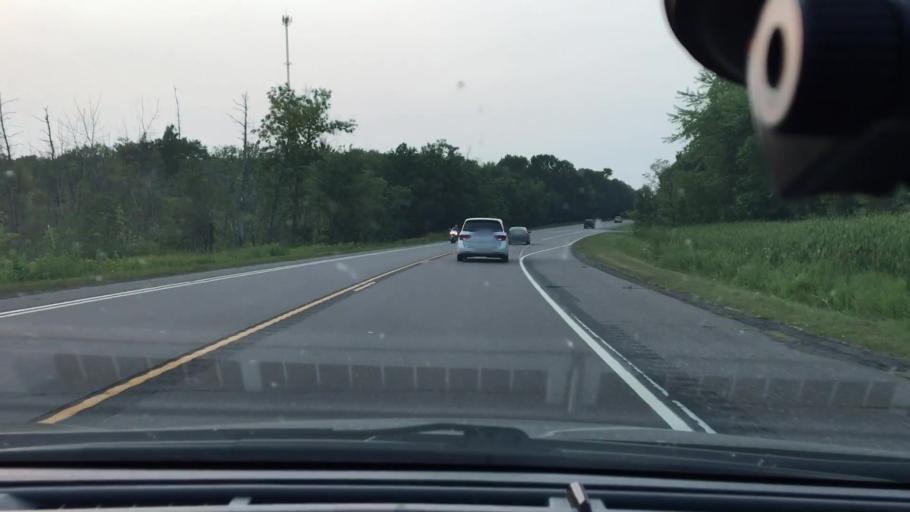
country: US
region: Minnesota
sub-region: Mille Lacs County
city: Vineland
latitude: 46.1138
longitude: -93.6588
